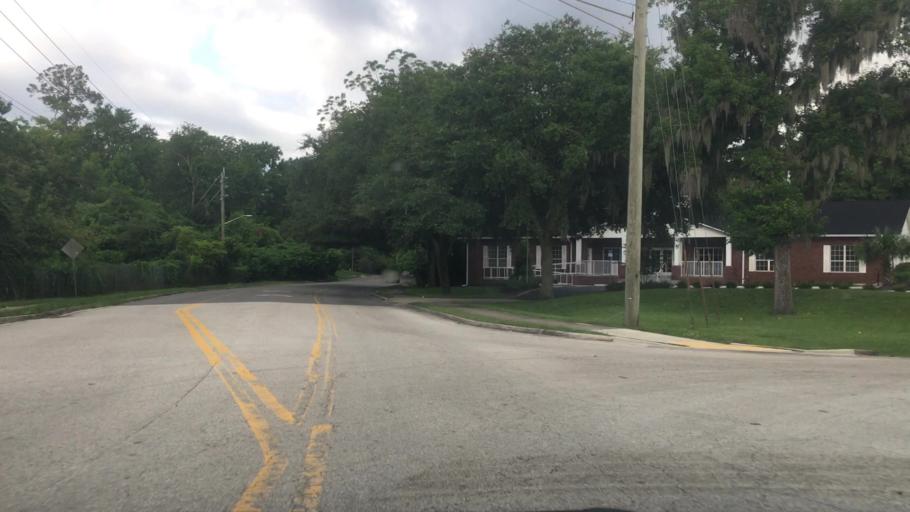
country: US
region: Florida
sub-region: Duval County
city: Jacksonville
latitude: 30.2940
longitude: -81.6101
